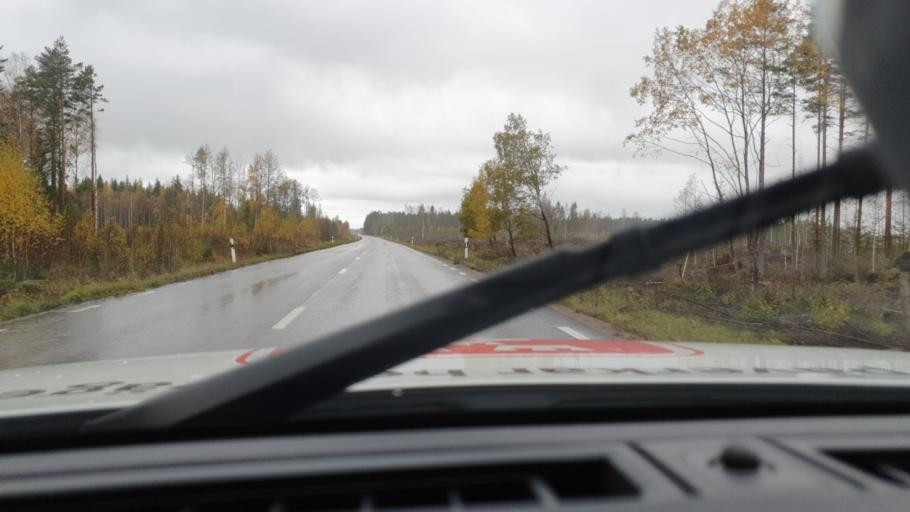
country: SE
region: Uppsala
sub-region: Alvkarleby Kommun
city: AElvkarleby
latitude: 60.5455
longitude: 17.5327
